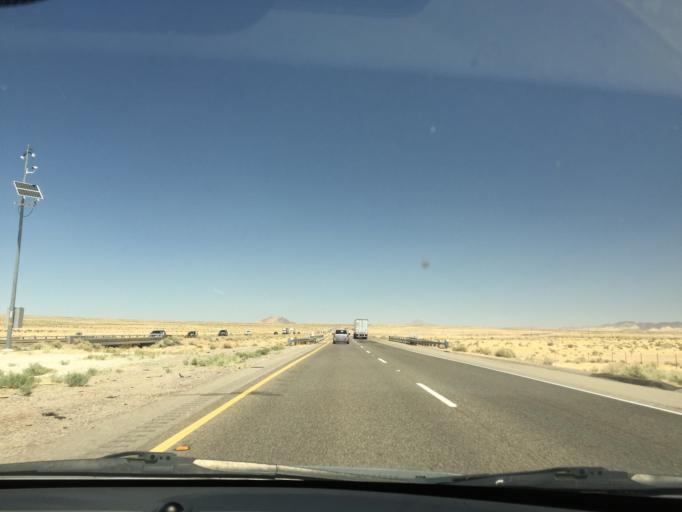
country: US
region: California
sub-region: San Bernardino County
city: Fort Irwin
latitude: 34.9921
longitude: -116.5792
